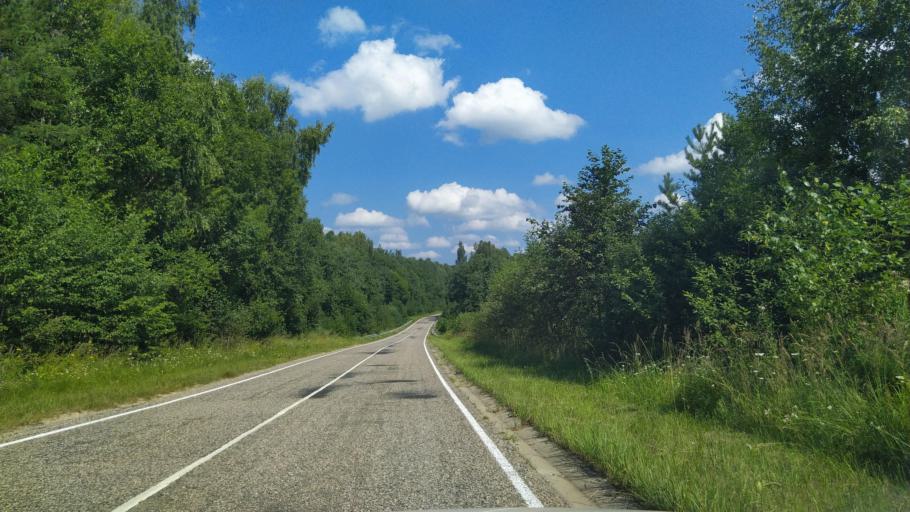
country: RU
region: Pskov
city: Pushkinskiye Gory
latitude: 57.0622
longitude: 28.9486
